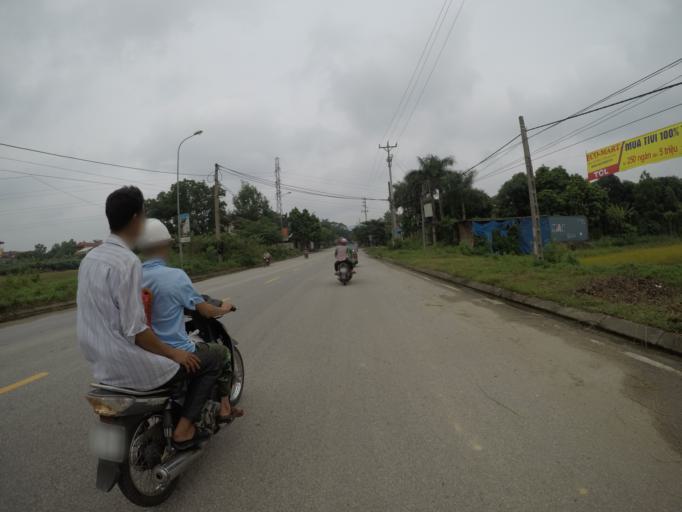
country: VN
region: Ha Noi
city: Soc Son
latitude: 21.2762
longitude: 105.8485
